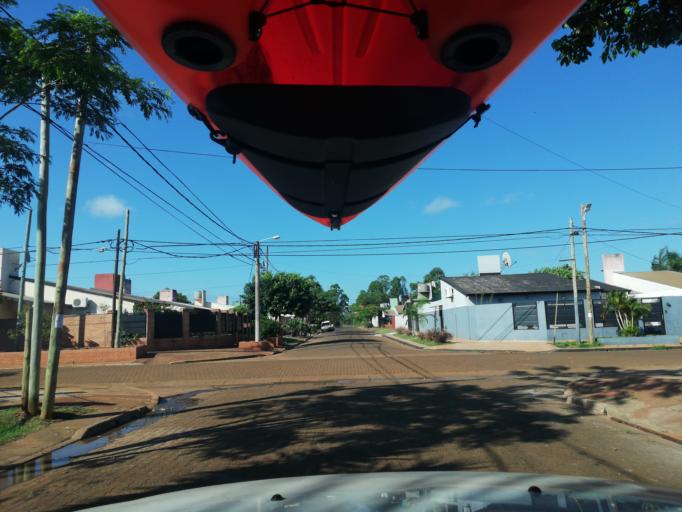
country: AR
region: Misiones
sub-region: Departamento de Capital
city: Posadas
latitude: -27.4248
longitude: -55.9390
